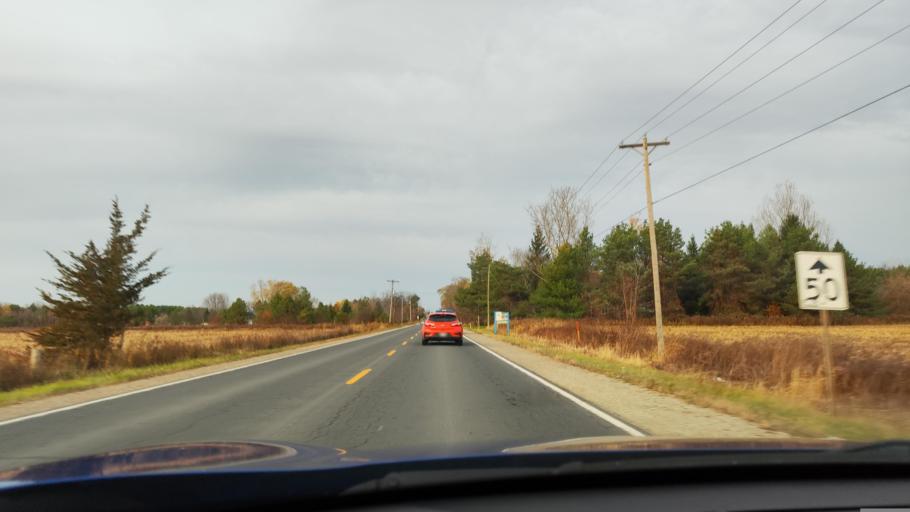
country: CA
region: Ontario
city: Angus
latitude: 44.3609
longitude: -79.9601
